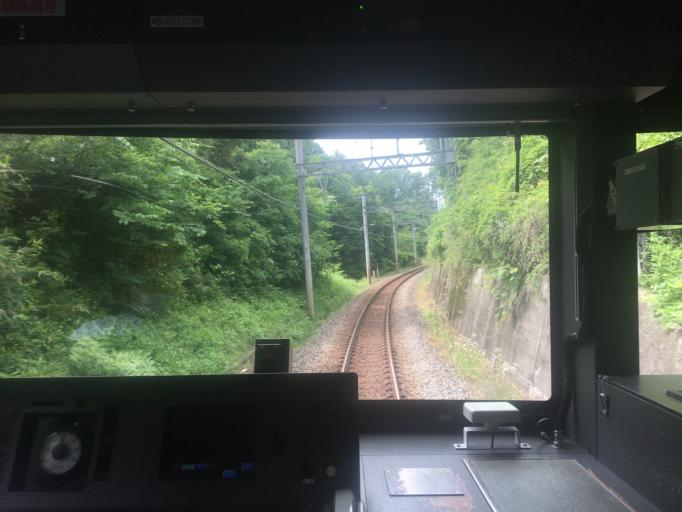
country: JP
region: Saitama
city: Ogawa
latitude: 36.0545
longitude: 139.2928
